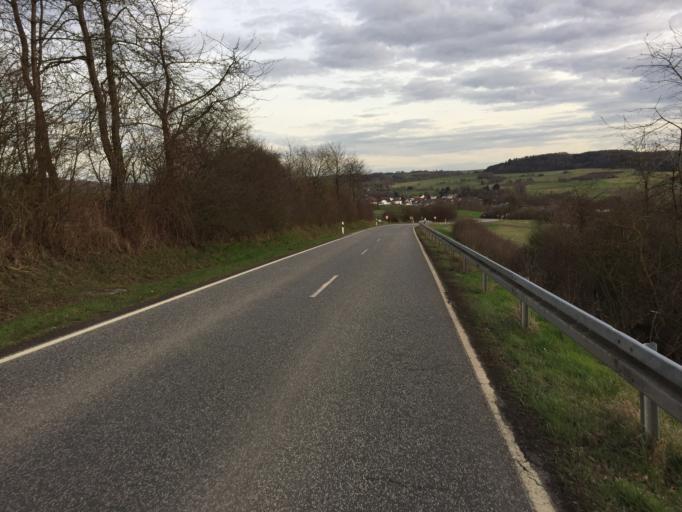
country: DE
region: Hesse
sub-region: Regierungsbezirk Giessen
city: Rabenau
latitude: 50.6857
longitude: 8.8478
